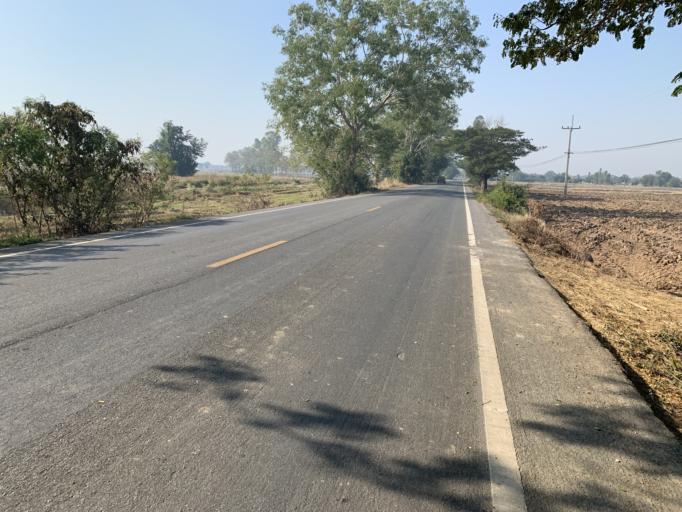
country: TH
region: Uttaradit
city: Phichai
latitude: 17.3561
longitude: 100.0931
